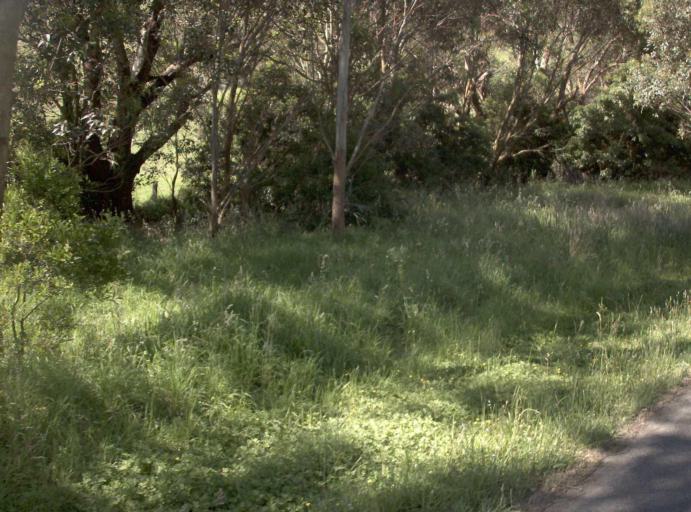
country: AU
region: Victoria
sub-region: Latrobe
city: Morwell
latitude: -38.6529
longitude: 146.3027
